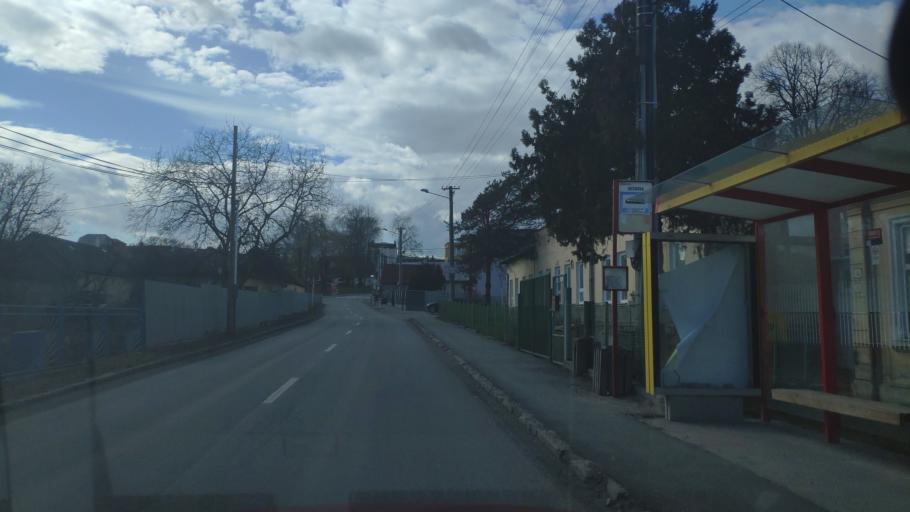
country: SK
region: Kosicky
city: Kosice
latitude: 48.6746
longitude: 21.2681
